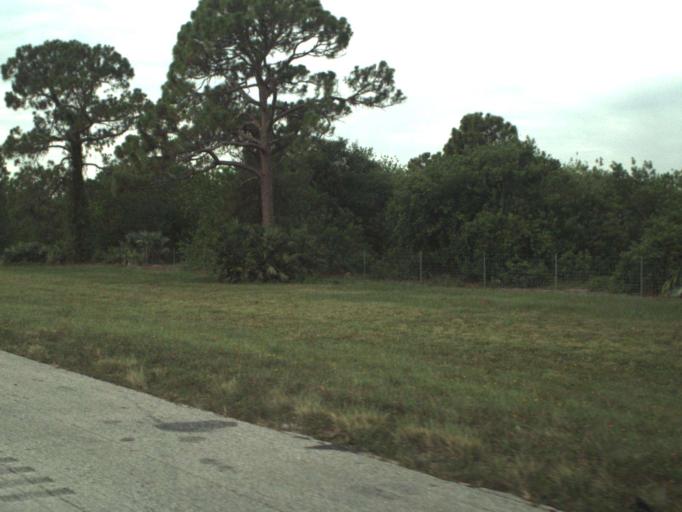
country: US
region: Florida
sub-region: Martin County
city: Palm City
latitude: 27.1695
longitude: -80.3945
